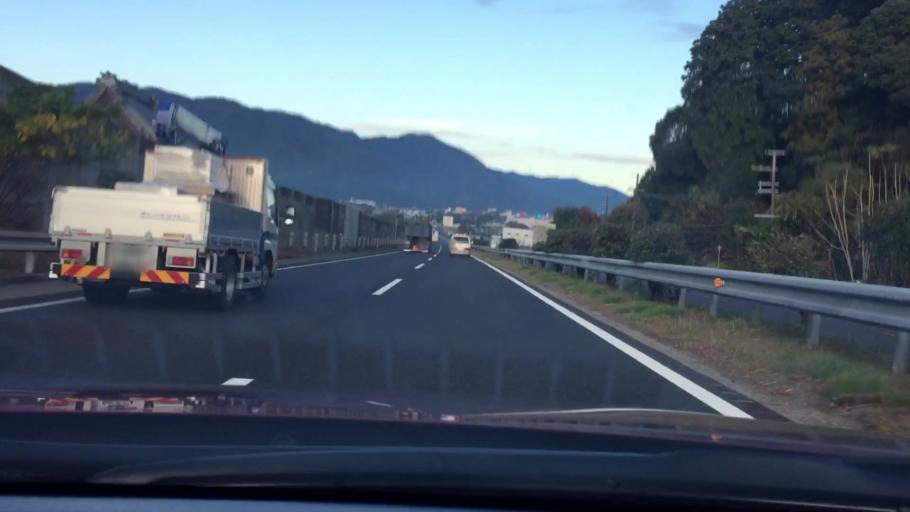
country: JP
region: Hyogo
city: Yamazakicho-nakabirose
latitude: 34.9966
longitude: 134.5605
